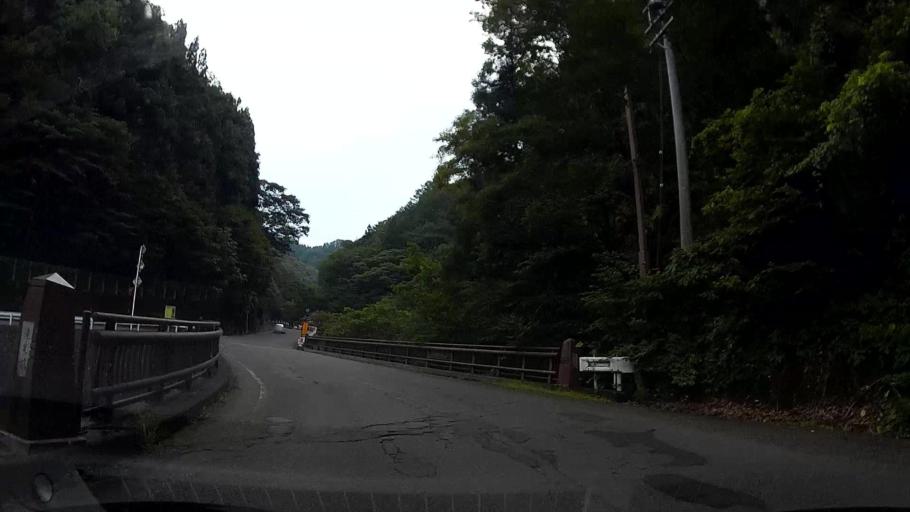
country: JP
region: Nagano
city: Iiyama
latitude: 36.8256
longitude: 138.4262
